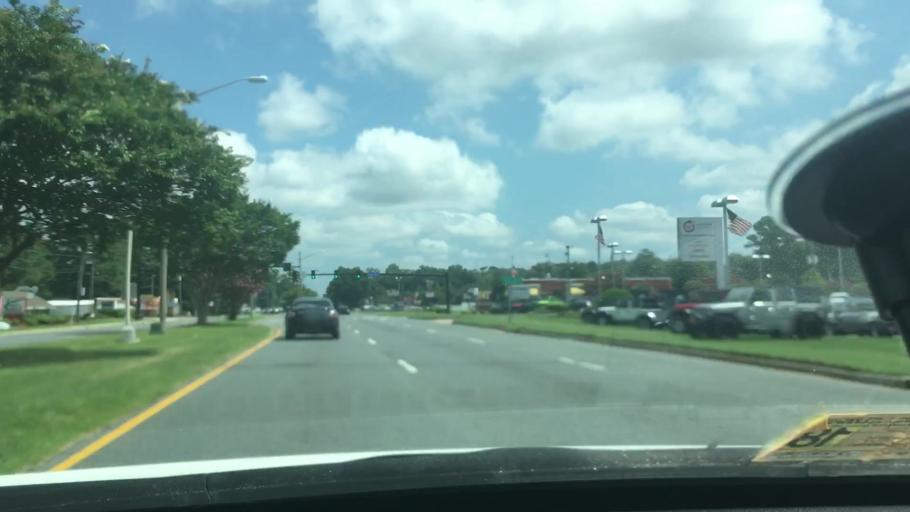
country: US
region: Virginia
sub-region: City of Chesapeake
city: Chesapeake
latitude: 36.7993
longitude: -76.2319
